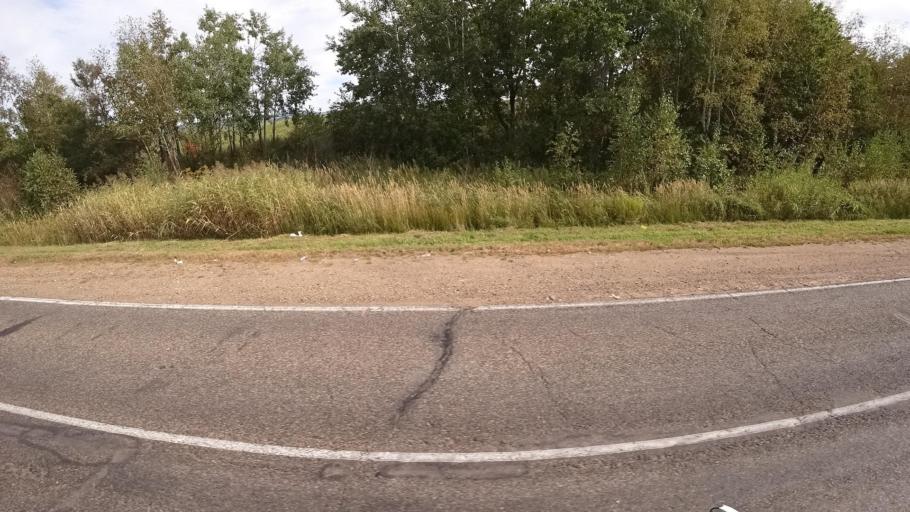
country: RU
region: Primorskiy
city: Dostoyevka
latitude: 44.3243
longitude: 133.4888
